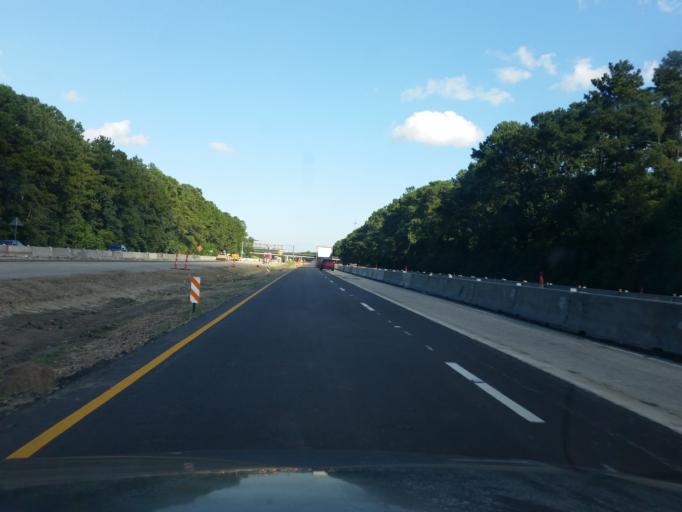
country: US
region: Louisiana
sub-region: Saint Tammany Parish
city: Slidell
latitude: 30.3029
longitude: -89.7297
